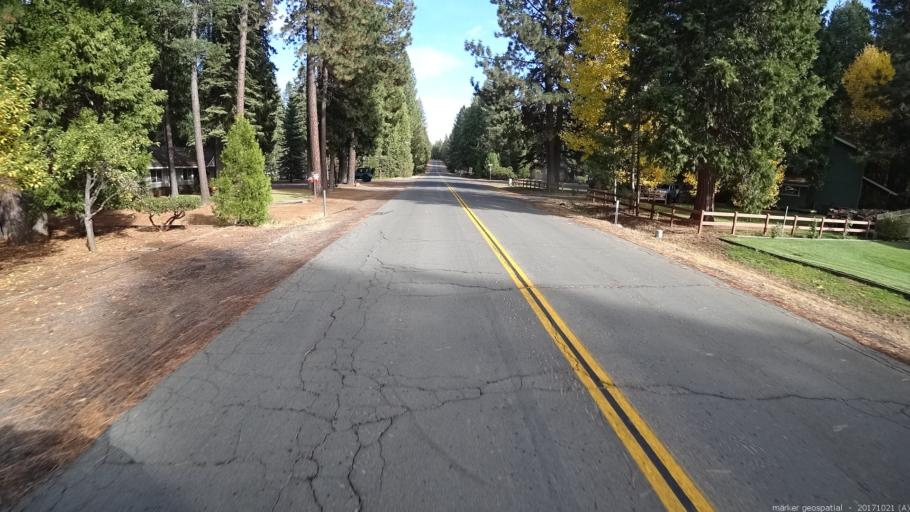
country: US
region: California
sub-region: Shasta County
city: Burney
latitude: 40.8719
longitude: -121.6686
